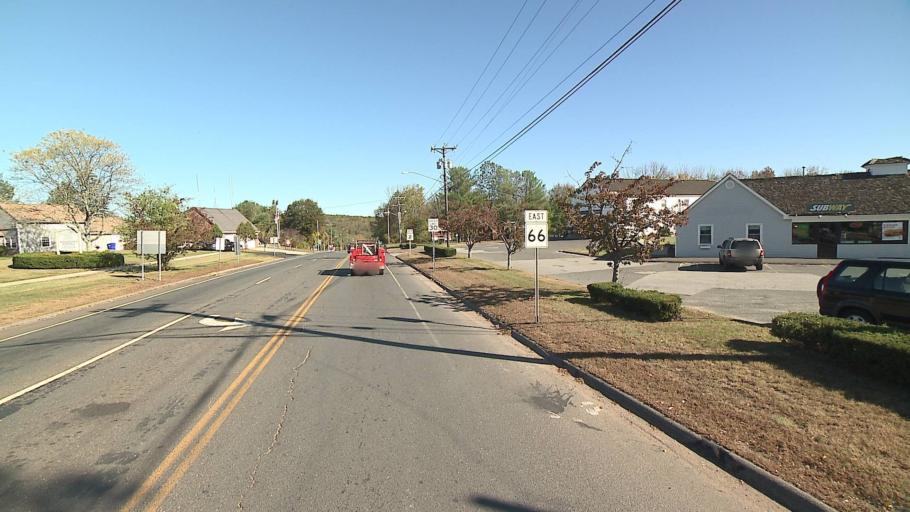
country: US
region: Connecticut
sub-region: Hartford County
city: Terramuggus
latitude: 41.6318
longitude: -72.4597
